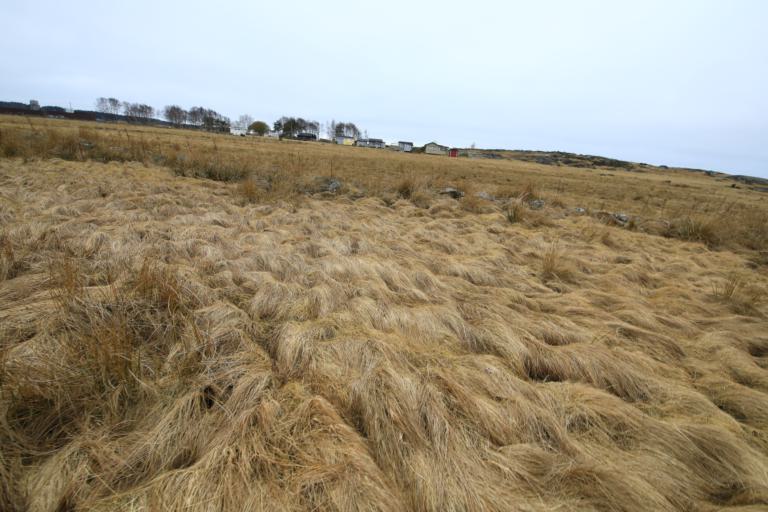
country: SE
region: Halland
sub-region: Kungsbacka Kommun
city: Frillesas
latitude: 57.2460
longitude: 12.1253
